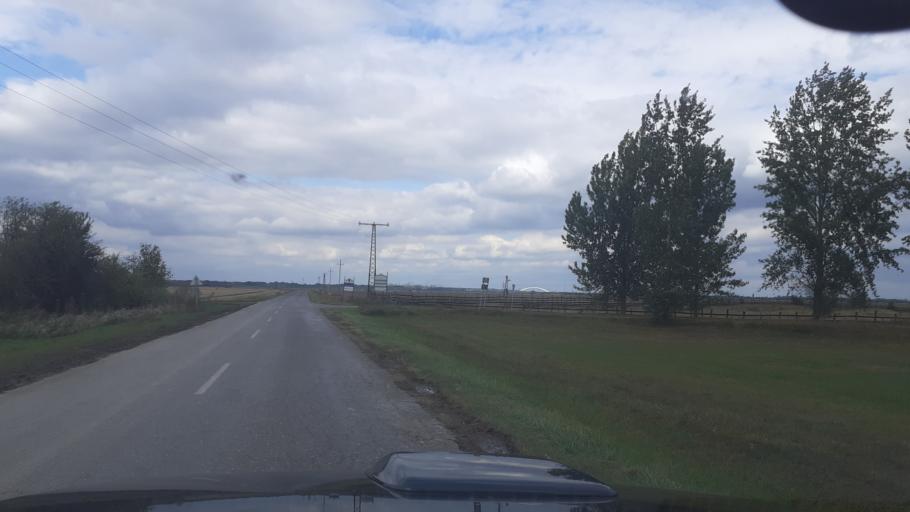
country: HU
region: Bacs-Kiskun
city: Apostag
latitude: 46.8420
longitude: 18.9508
